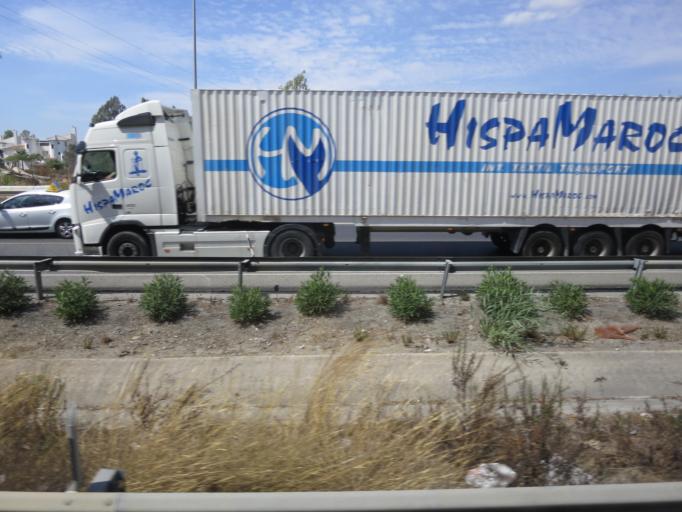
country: ES
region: Andalusia
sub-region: Provincia de Malaga
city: Marbella
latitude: 36.5092
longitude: -4.9483
